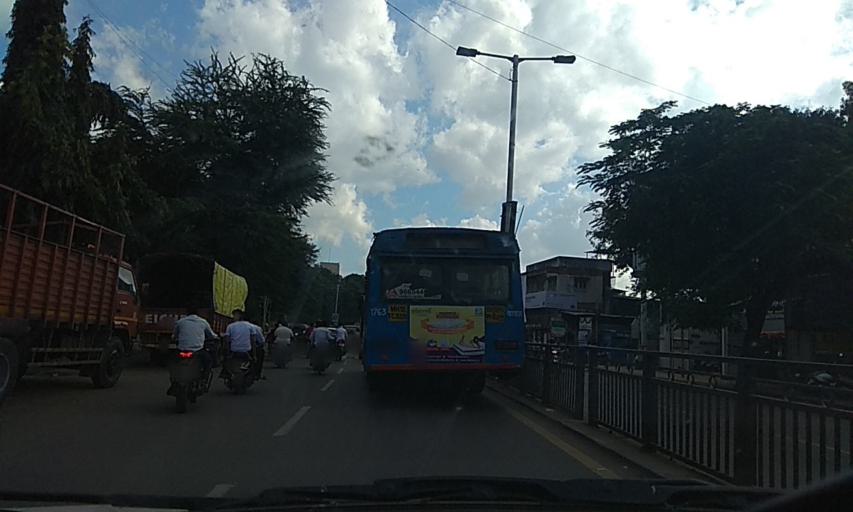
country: IN
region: Maharashtra
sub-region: Pune Division
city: Pune
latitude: 18.5076
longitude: 73.8684
